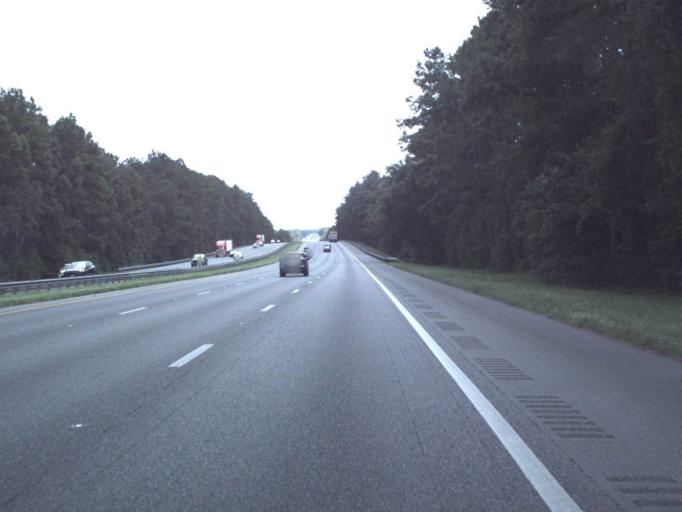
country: US
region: Florida
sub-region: Alachua County
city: High Springs
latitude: 29.9421
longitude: -82.5656
